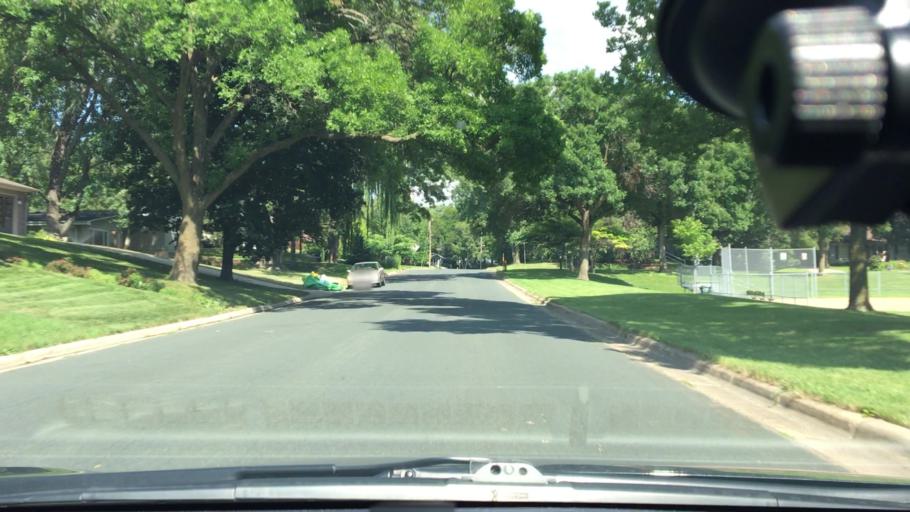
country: US
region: Minnesota
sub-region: Hennepin County
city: Golden Valley
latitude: 44.9973
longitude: -93.3842
